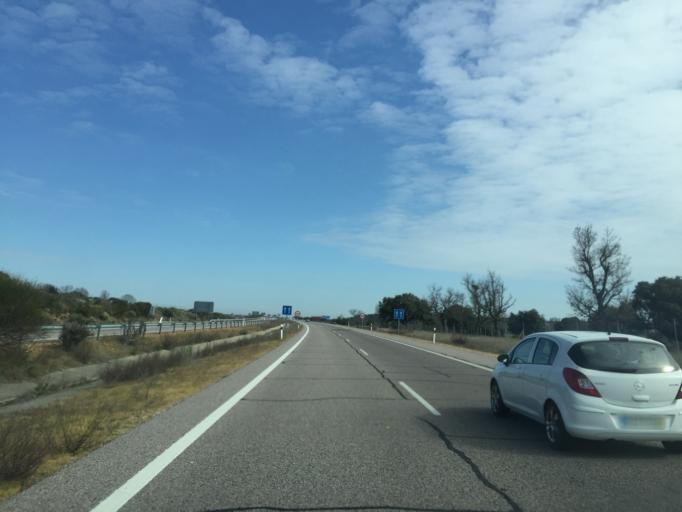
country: ES
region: Castille and Leon
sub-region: Provincia de Salamanca
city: Tenebron
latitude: 40.6728
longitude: -6.4303
